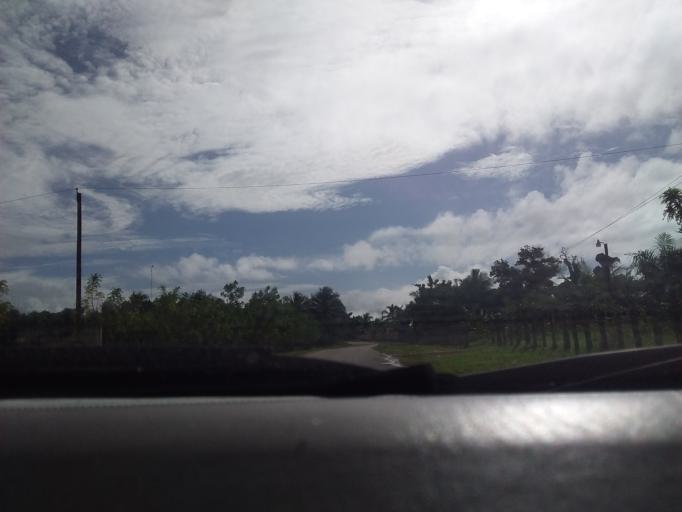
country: DO
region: Santo Domingo
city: Guerra
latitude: 18.5589
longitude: -69.7854
